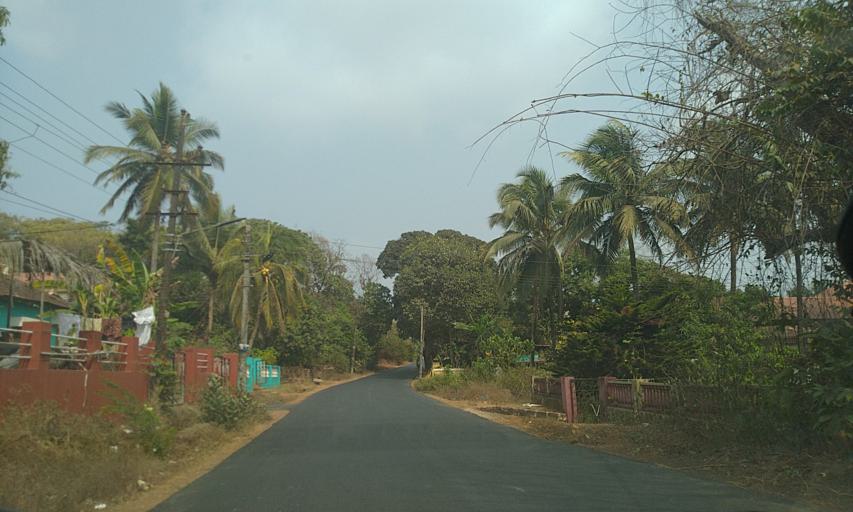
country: IN
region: Goa
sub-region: South Goa
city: Raia
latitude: 15.3076
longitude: 73.9680
